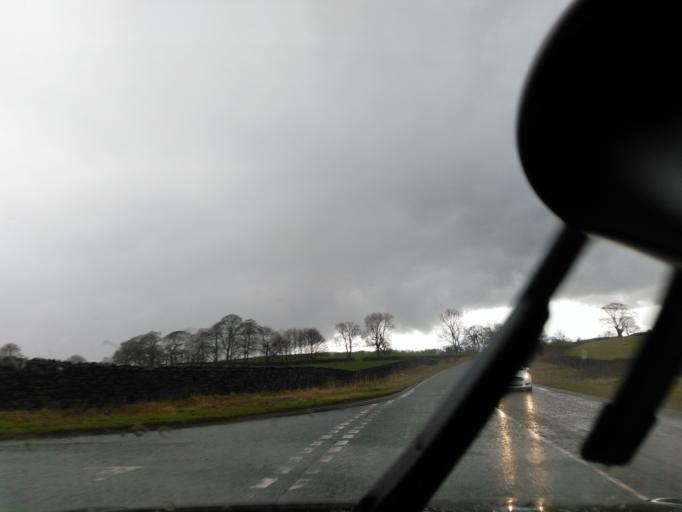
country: GB
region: England
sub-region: North Yorkshire
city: Embsay
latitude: 53.9770
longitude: -1.9537
